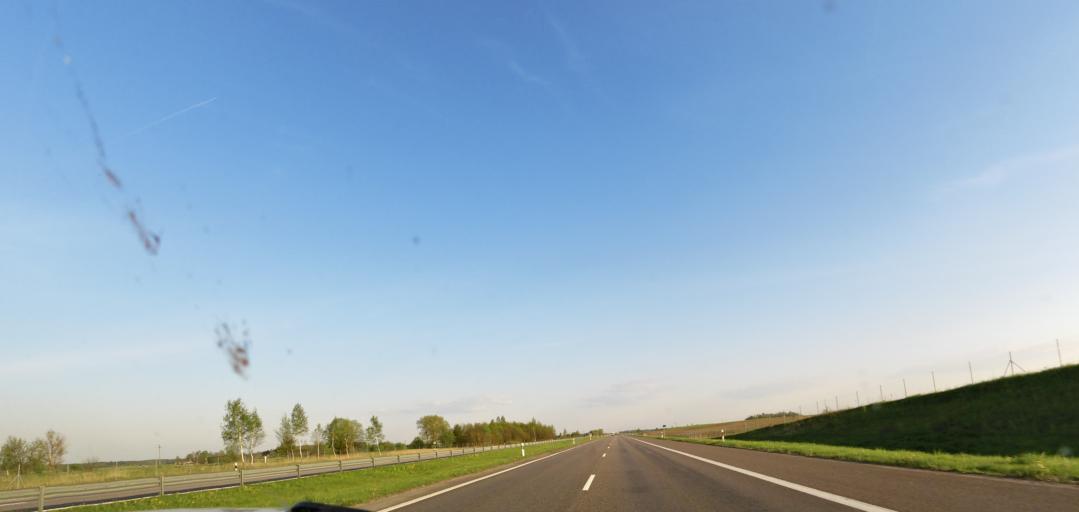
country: LT
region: Vilnius County
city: Ukmerge
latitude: 55.1674
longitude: 24.8160
